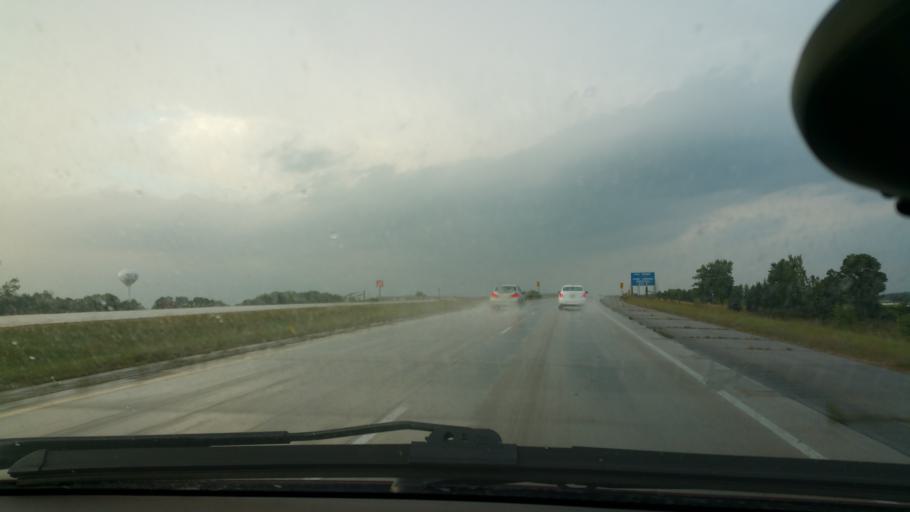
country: US
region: Minnesota
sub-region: Freeborn County
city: Albert Lea
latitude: 43.6467
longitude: -93.3230
